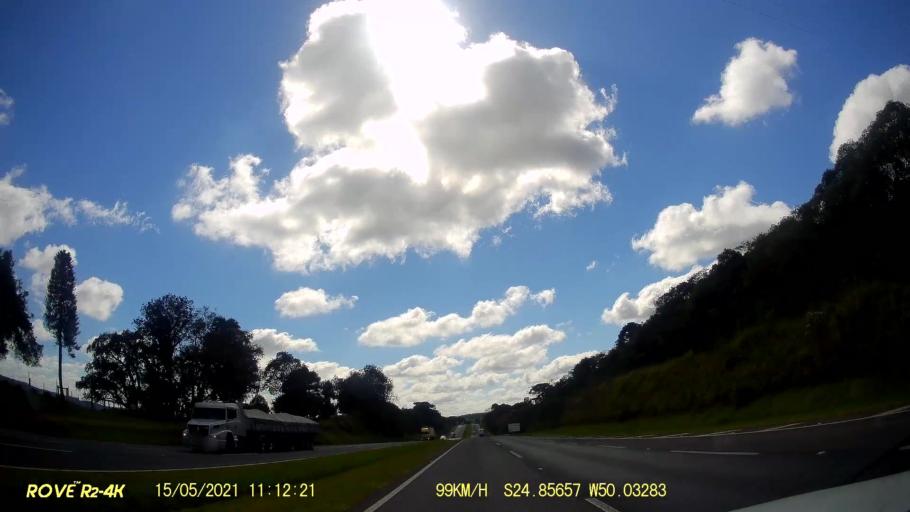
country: BR
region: Parana
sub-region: Castro
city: Castro
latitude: -24.8566
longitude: -50.0329
